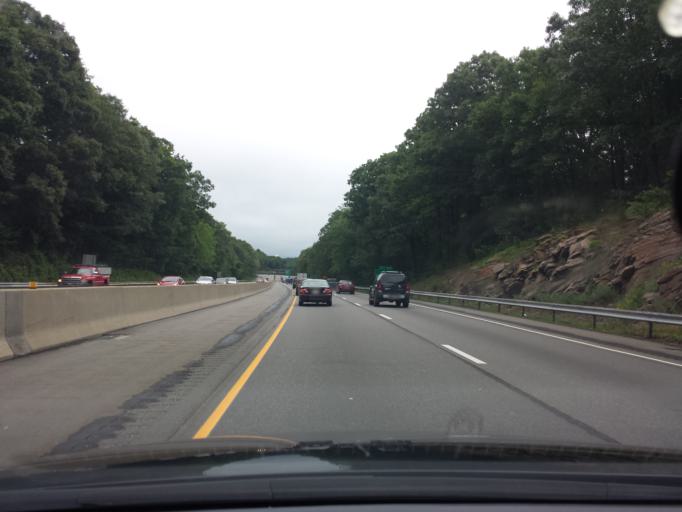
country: US
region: Connecticut
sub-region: Middlesex County
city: Clinton
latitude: 41.2904
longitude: -72.4989
